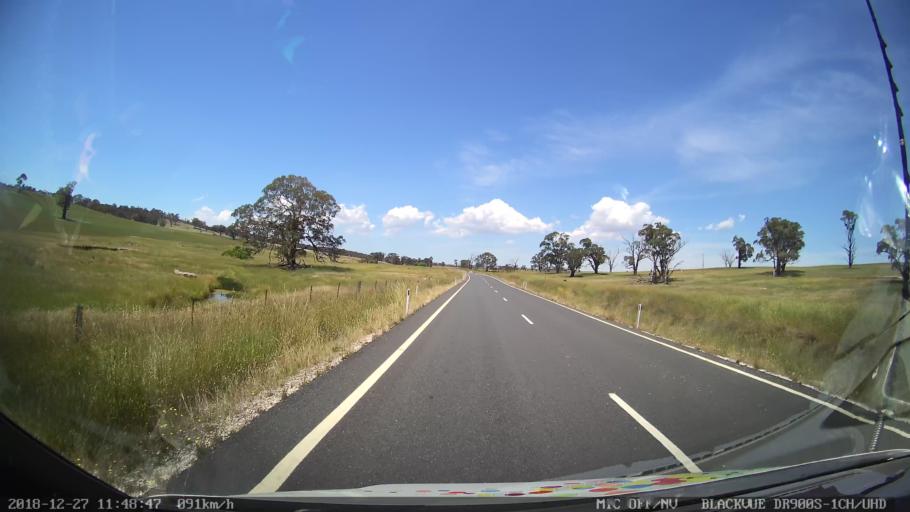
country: AU
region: New South Wales
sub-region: Bathurst Regional
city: Perthville
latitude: -33.6111
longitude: 149.4353
